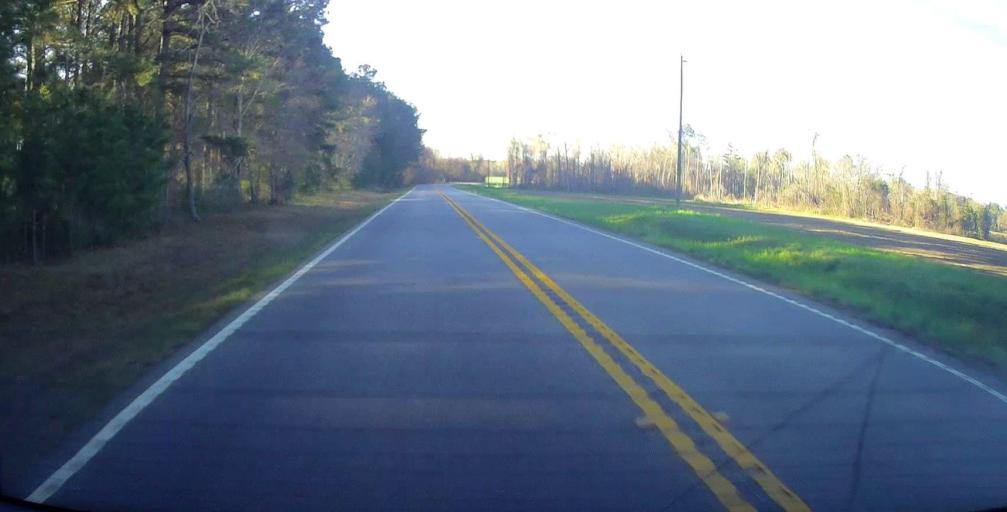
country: US
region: Georgia
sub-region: Pulaski County
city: Hawkinsville
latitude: 32.1692
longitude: -83.3610
